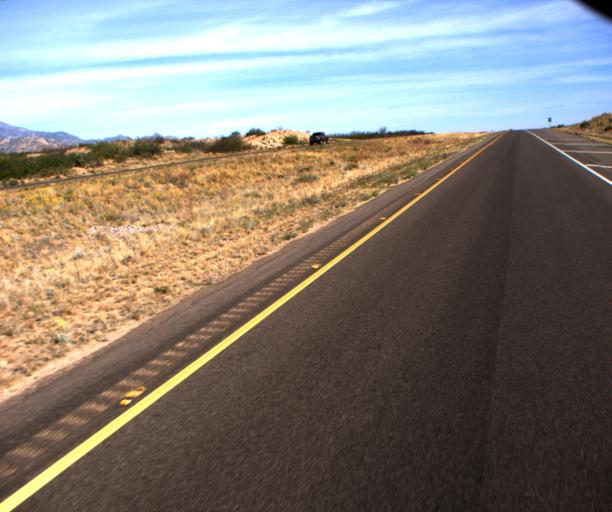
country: US
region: Arizona
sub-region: Graham County
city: Swift Trail Junction
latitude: 32.5882
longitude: -109.6835
